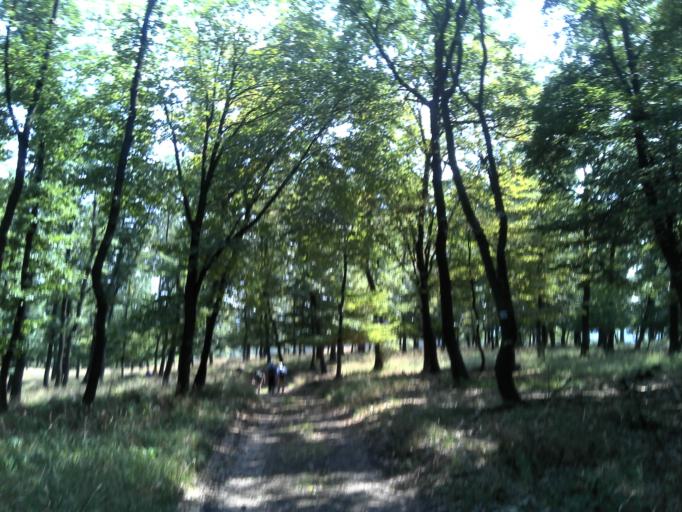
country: HU
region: Komarom-Esztergom
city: Oroszlany
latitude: 47.4399
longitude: 18.3778
